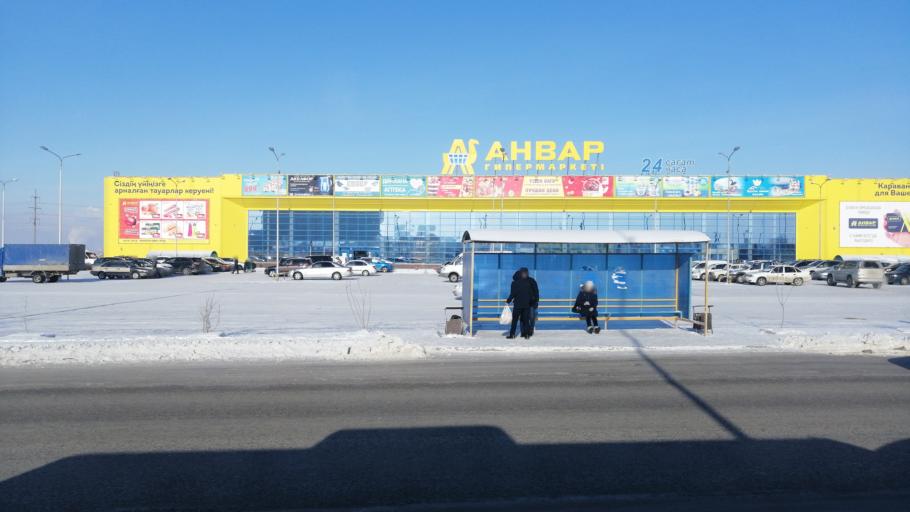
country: KZ
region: Aqtoebe
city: Aqtobe
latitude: 50.2984
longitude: 57.1916
